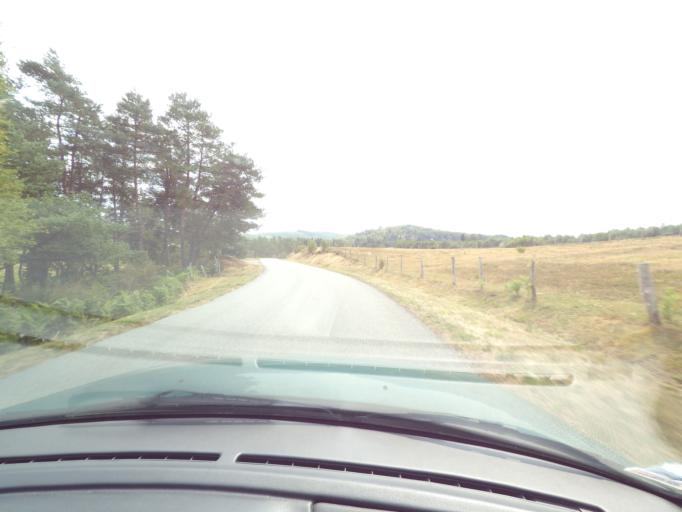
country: FR
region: Limousin
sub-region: Departement de la Correze
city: Bugeat
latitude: 45.7050
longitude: 2.0264
